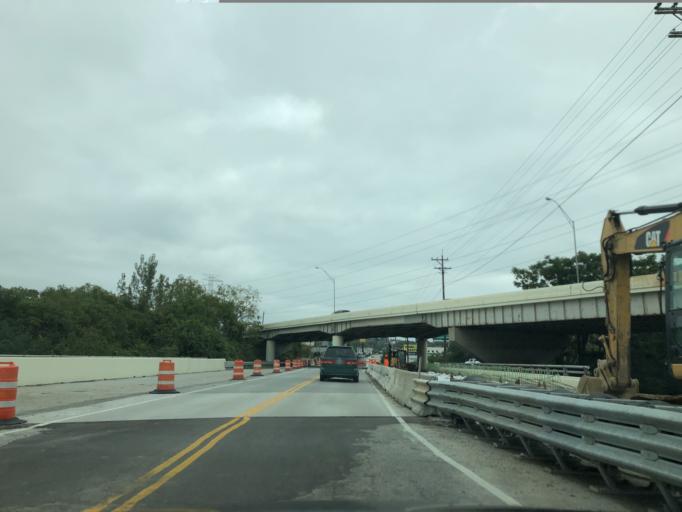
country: US
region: Ohio
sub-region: Hamilton County
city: Lockland
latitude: 39.2121
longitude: -84.4582
